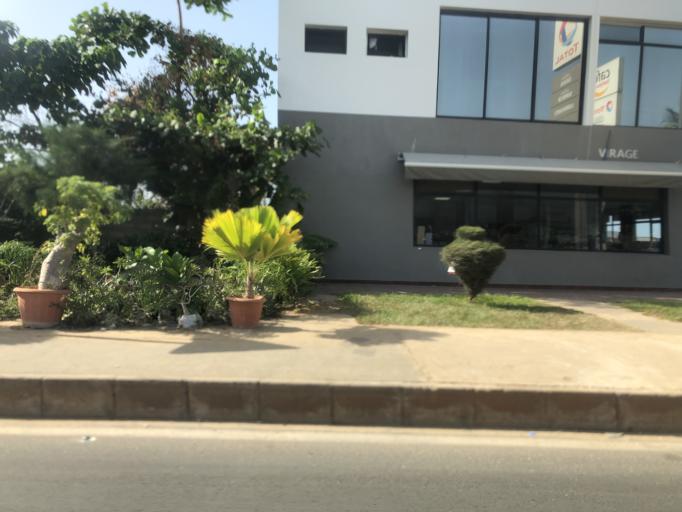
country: SN
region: Dakar
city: Mermoz Boabab
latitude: 14.7518
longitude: -17.5009
